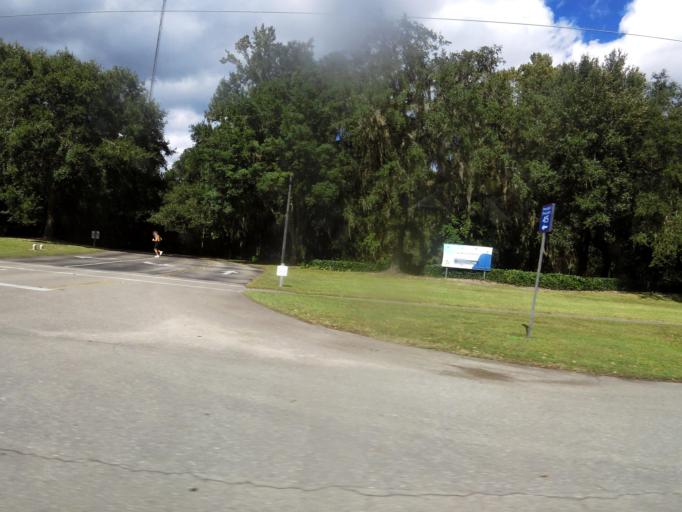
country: US
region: Florida
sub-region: Alachua County
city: Alachua
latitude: 29.7034
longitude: -82.3856
